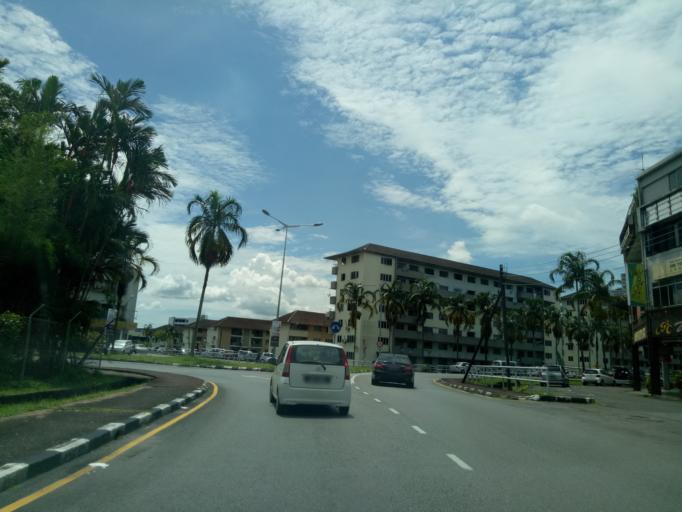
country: MY
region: Sarawak
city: Kuching
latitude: 1.5524
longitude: 110.3548
